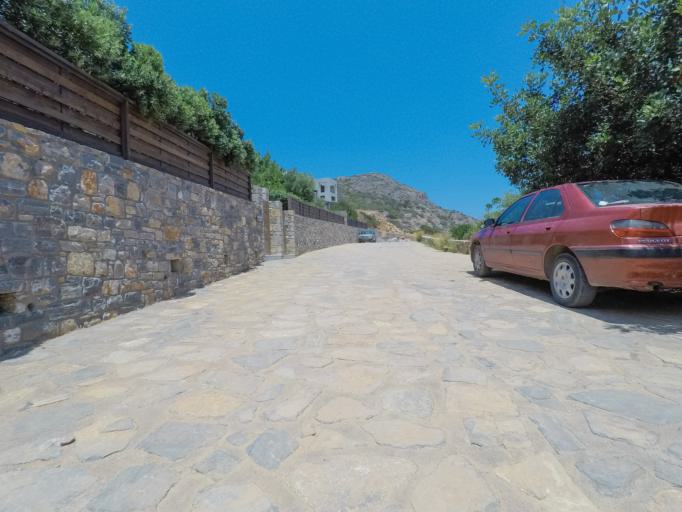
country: GR
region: Crete
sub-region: Nomos Lasithiou
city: Elounda
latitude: 35.3042
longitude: 25.7275
